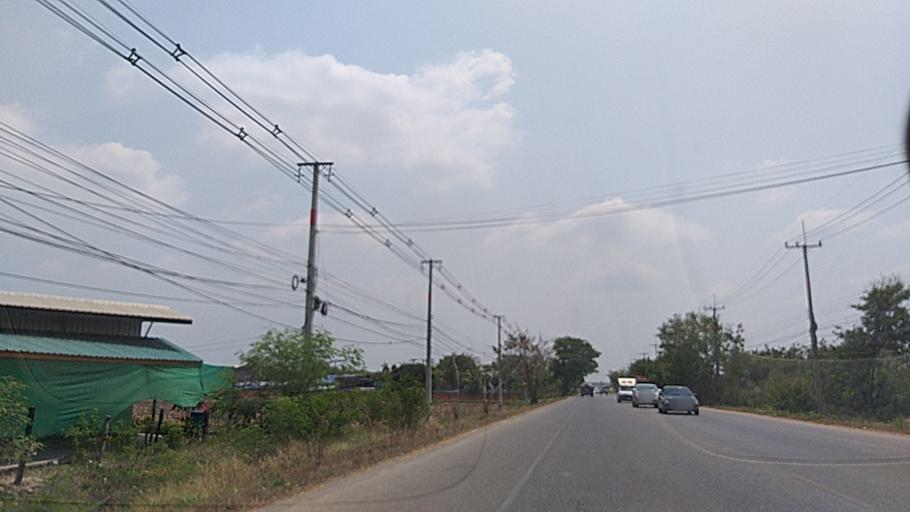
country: TH
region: Chachoengsao
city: Chachoengsao
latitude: 13.7538
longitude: 101.0761
